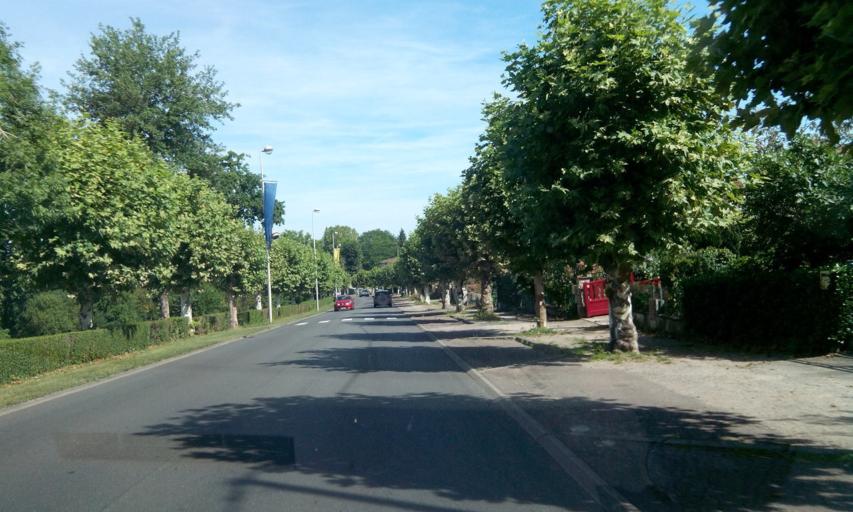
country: FR
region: Poitou-Charentes
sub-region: Departement de la Charente
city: Confolens
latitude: 46.0070
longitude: 0.6725
